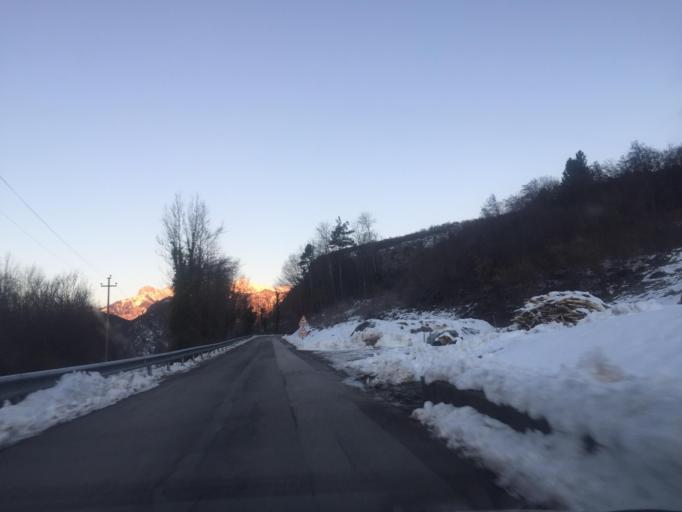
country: IT
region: Friuli Venezia Giulia
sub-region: Provincia di Udine
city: Villa Santina
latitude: 46.4192
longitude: 12.9168
